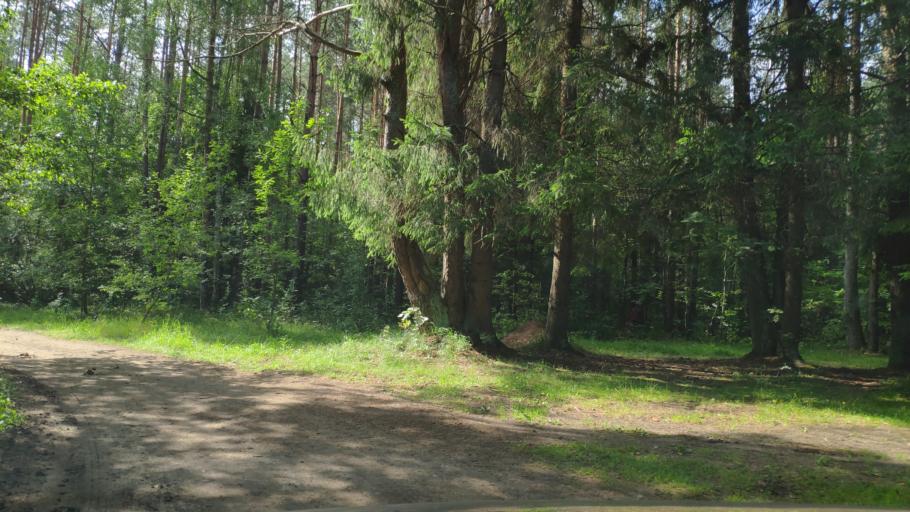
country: BY
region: Minsk
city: Zaslawye
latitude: 53.9742
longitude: 27.2893
